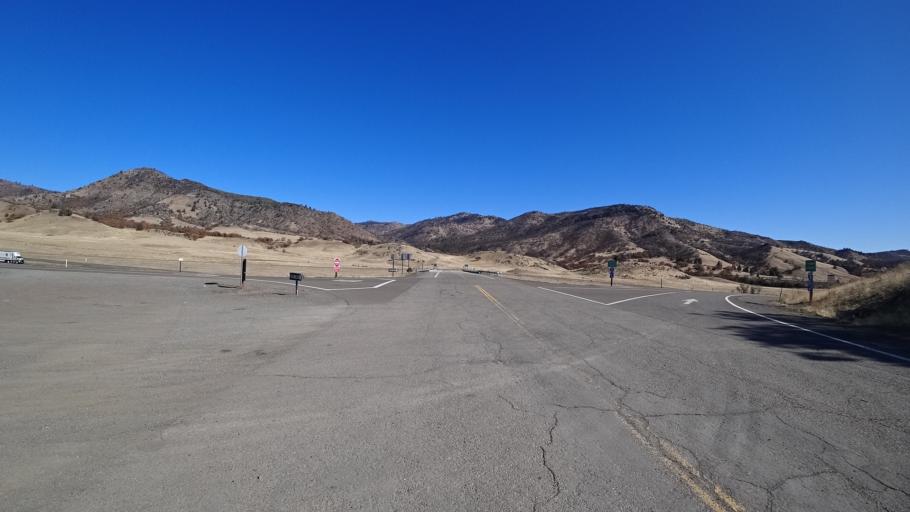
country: US
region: California
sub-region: Siskiyou County
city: Yreka
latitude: 41.9541
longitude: -122.5937
